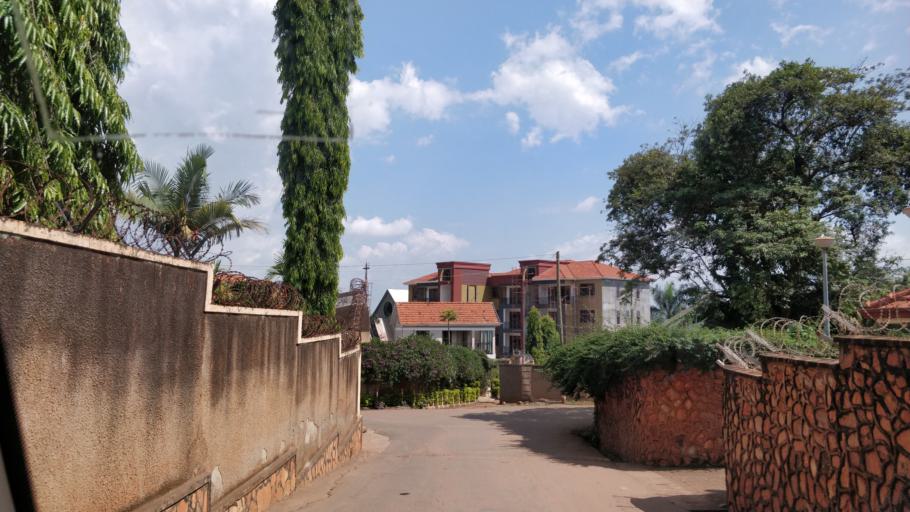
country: UG
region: Central Region
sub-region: Kampala District
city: Kampala
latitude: 0.2859
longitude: 32.6178
